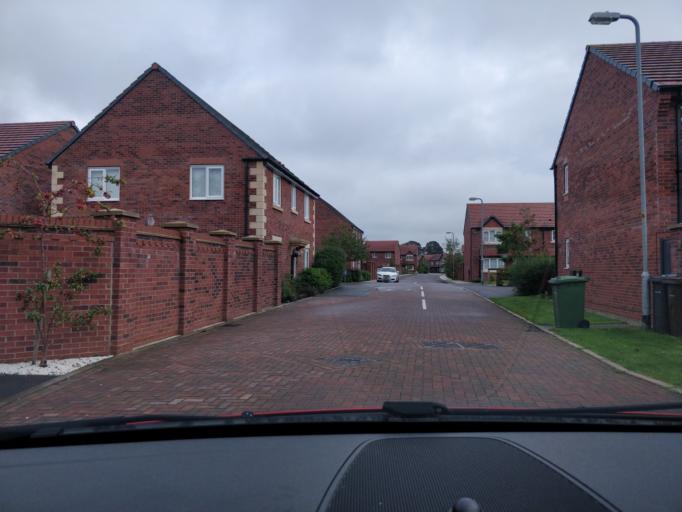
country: GB
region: England
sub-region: Sefton
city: Southport
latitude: 53.6069
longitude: -3.0253
